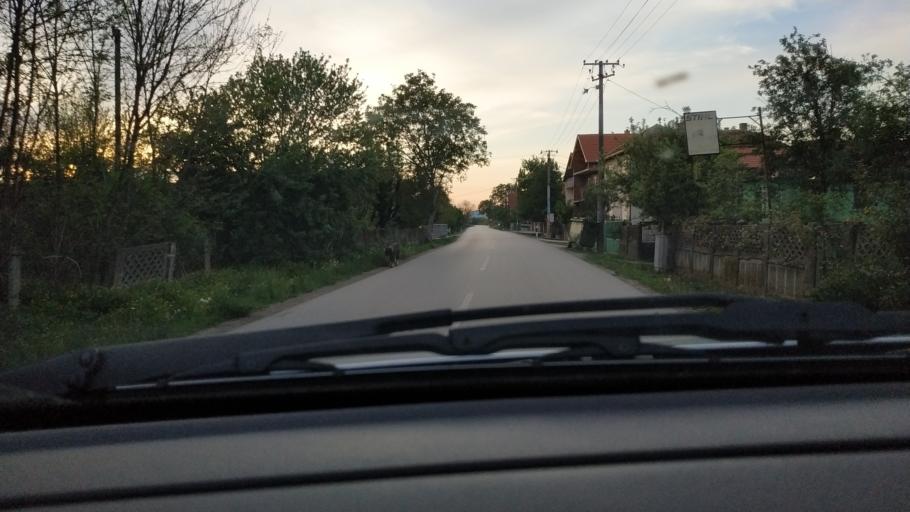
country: RS
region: Central Serbia
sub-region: Nisavski Okrug
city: Aleksinac
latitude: 43.5447
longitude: 21.6258
